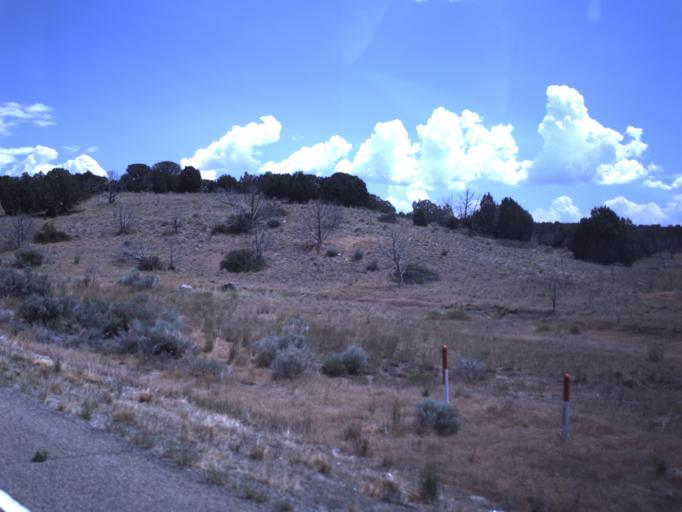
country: US
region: Utah
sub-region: Juab County
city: Nephi
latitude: 39.6616
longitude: -112.0617
